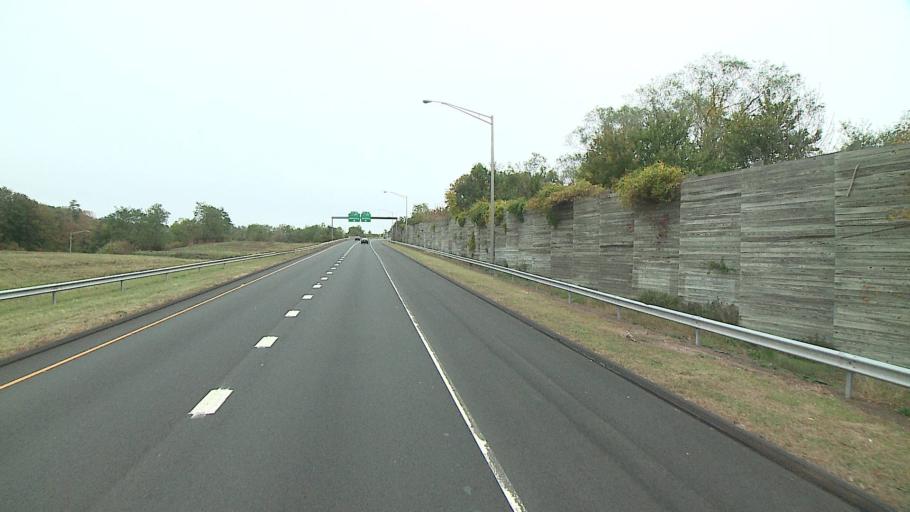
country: US
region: Connecticut
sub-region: Hartford County
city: West Hartford
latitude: 41.7215
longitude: -72.7706
